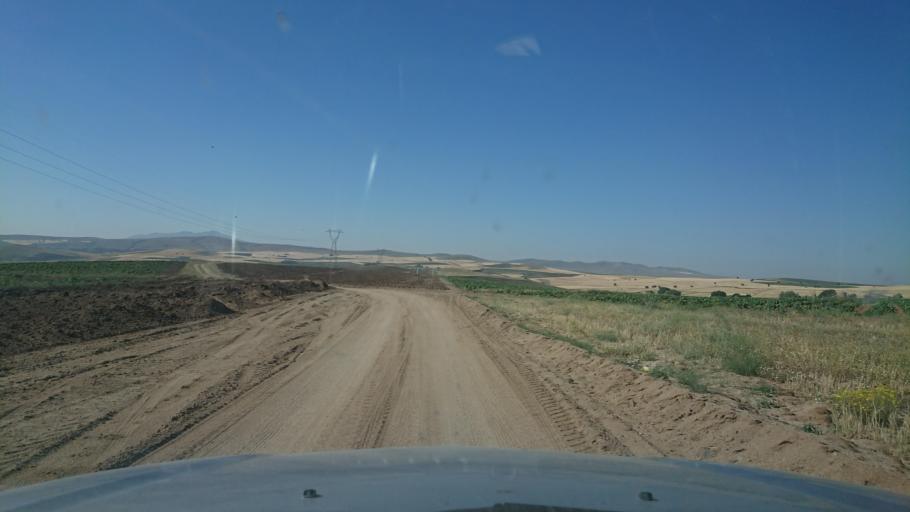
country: TR
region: Aksaray
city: Agacoren
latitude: 38.8377
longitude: 33.9443
